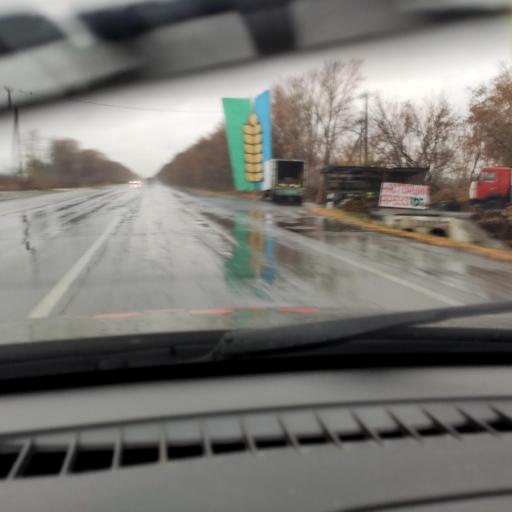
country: RU
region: Samara
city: Tol'yatti
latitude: 53.5966
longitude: 49.3253
